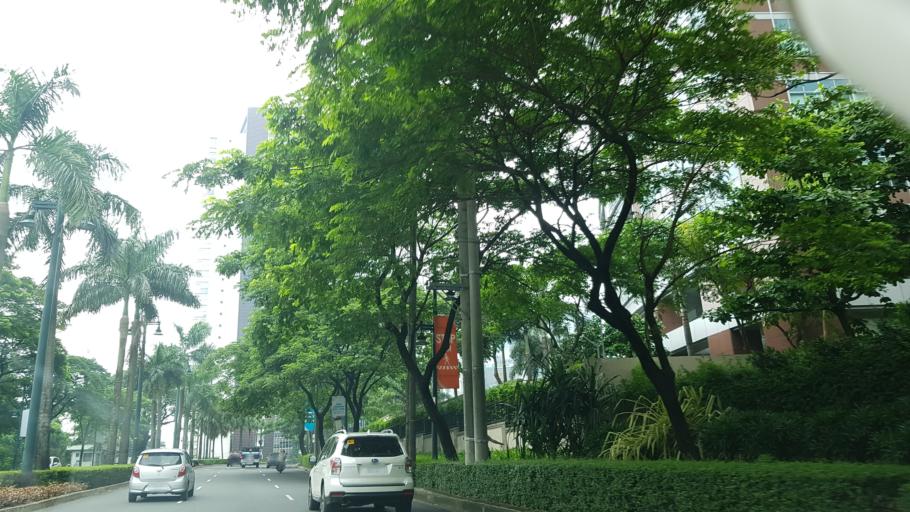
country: PH
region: Metro Manila
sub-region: Makati City
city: Makati City
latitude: 14.5436
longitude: 121.0462
